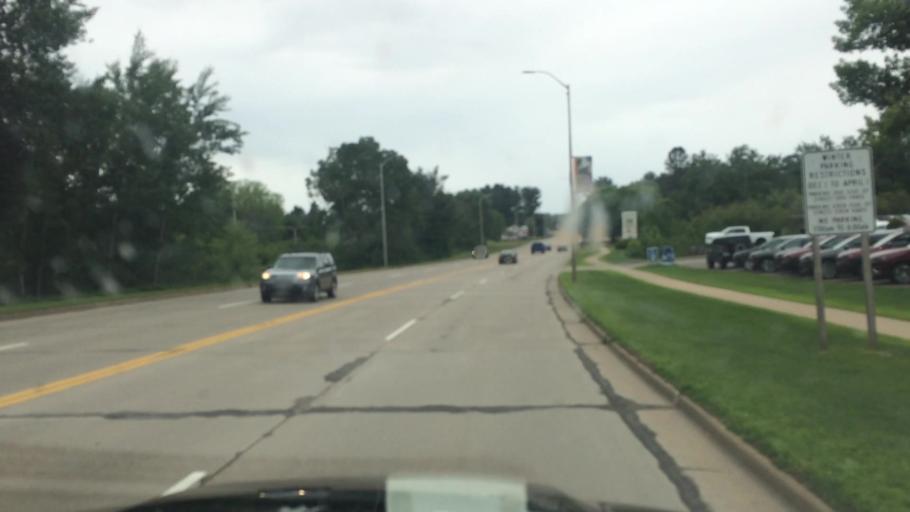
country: US
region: Wisconsin
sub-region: Lincoln County
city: Merrill
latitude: 45.1782
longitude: -89.6582
